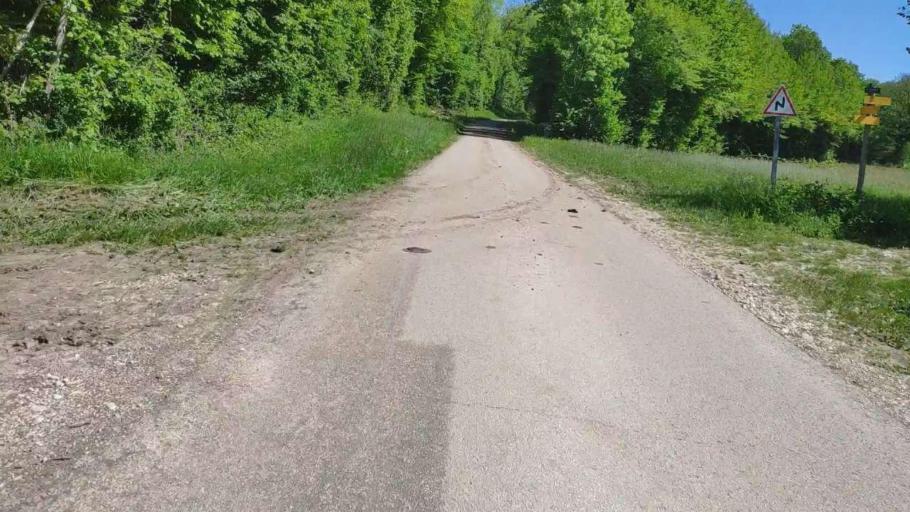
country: FR
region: Franche-Comte
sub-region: Departement du Jura
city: Poligny
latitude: 46.7424
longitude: 5.7726
